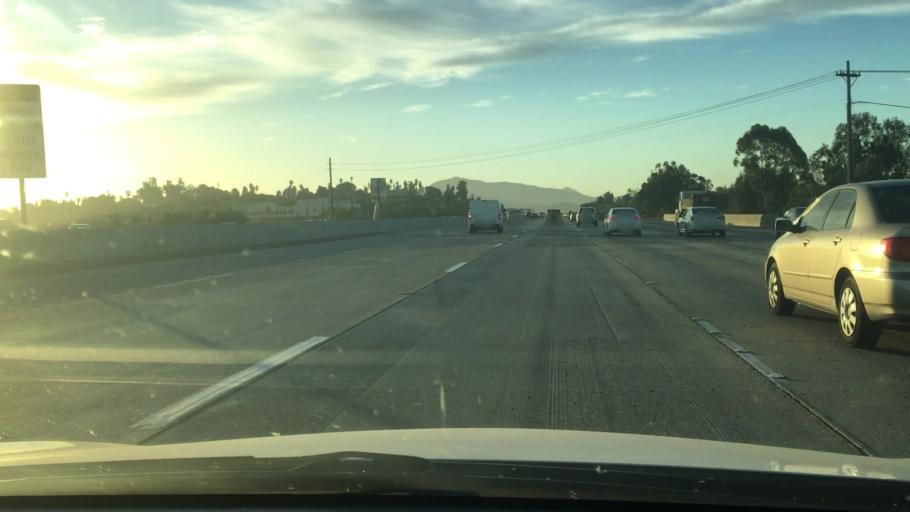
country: US
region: California
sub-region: San Diego County
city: Escondido
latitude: 33.0932
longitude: -117.0836
